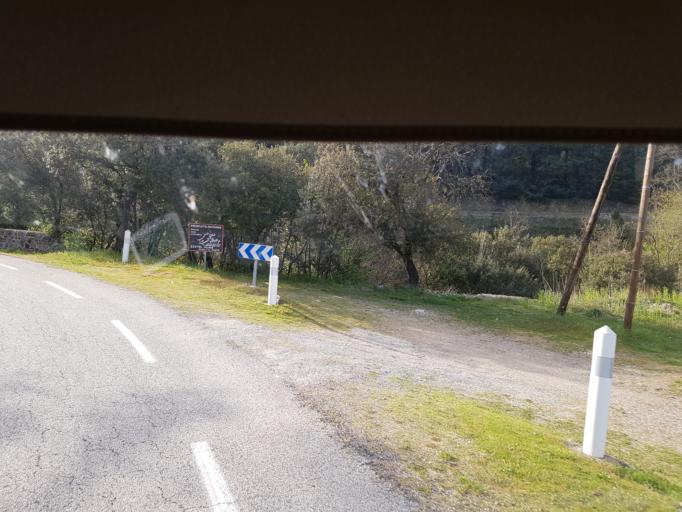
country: FR
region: Languedoc-Roussillon
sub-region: Departement du Gard
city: Branoux-les-Taillades
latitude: 44.3416
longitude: 3.9514
